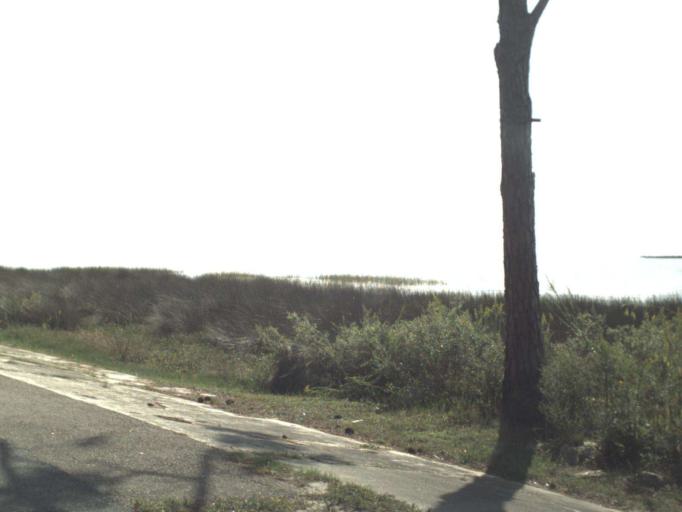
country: US
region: Florida
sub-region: Gulf County
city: Port Saint Joe
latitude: 29.7927
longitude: -85.3018
